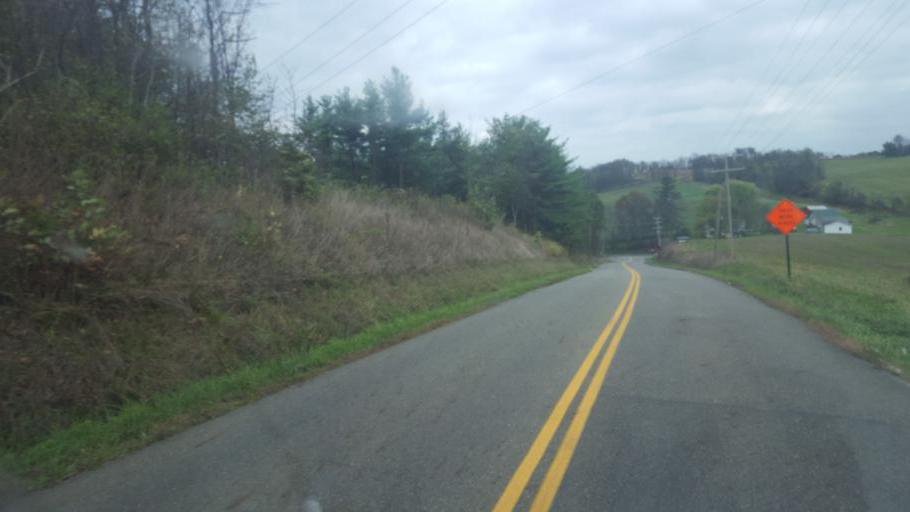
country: US
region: Ohio
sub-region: Carroll County
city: Carrollton
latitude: 40.5039
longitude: -81.1160
